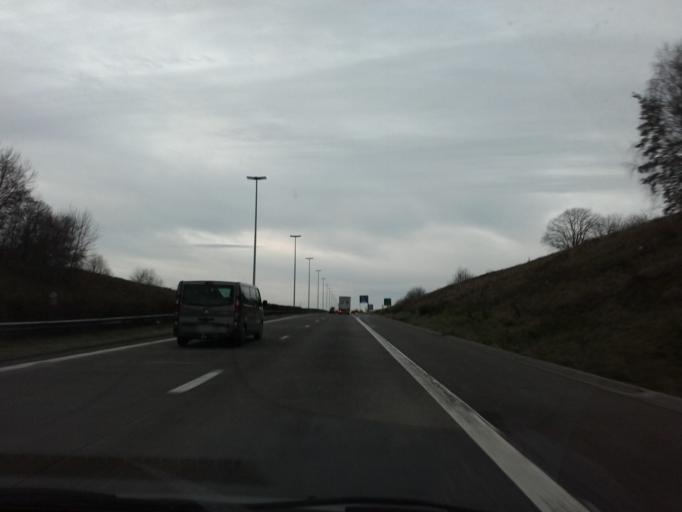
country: BE
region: Wallonia
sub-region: Province de Liege
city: Sprimont
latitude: 50.5049
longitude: 5.6938
